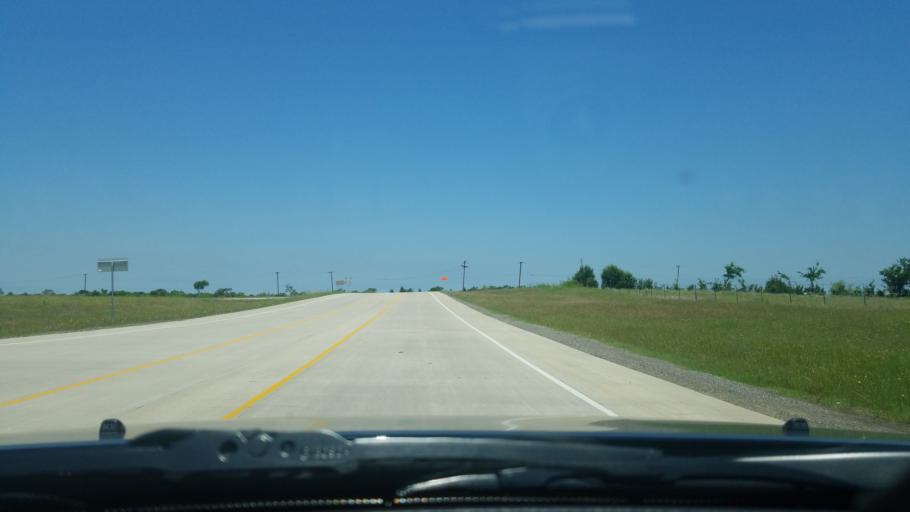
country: US
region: Texas
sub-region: Denton County
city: Krum
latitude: 33.2365
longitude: -97.2490
